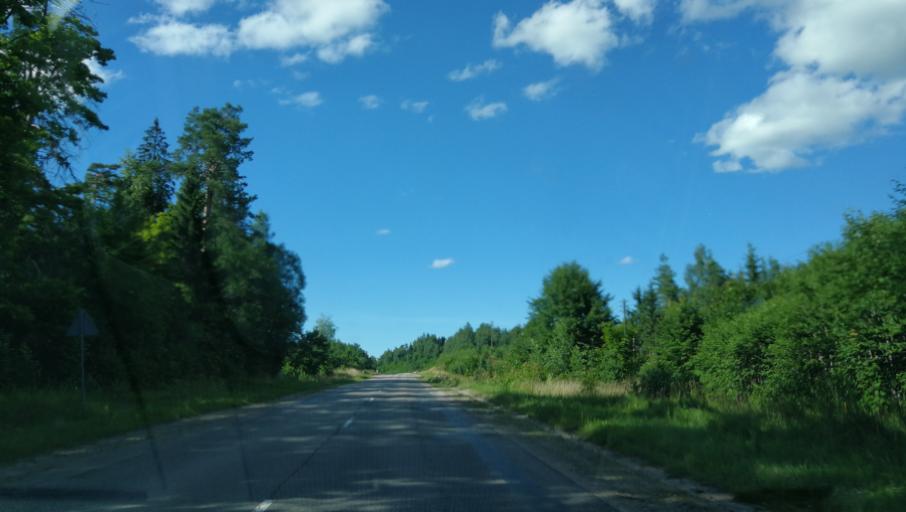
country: LV
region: Madonas Rajons
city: Madona
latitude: 56.8712
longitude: 26.1801
